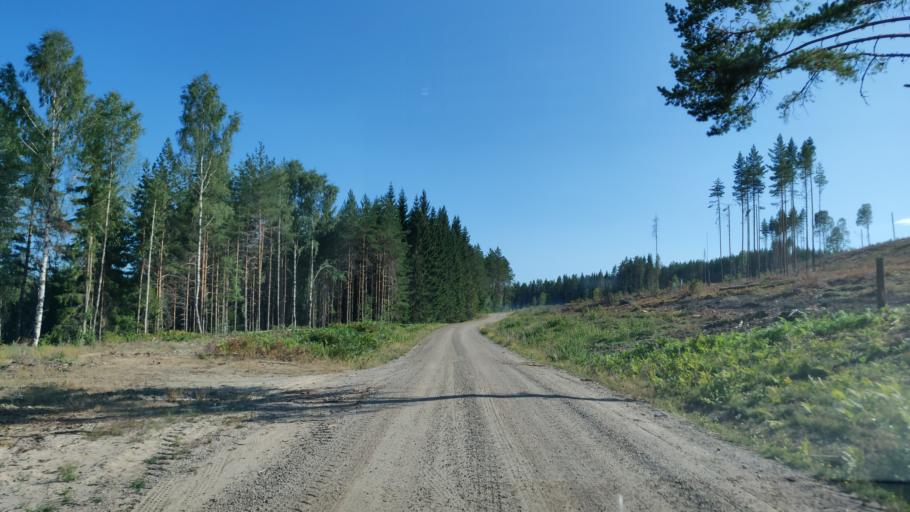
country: SE
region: Vaermland
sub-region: Hagfors Kommun
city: Ekshaerad
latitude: 60.1495
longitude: 13.5168
